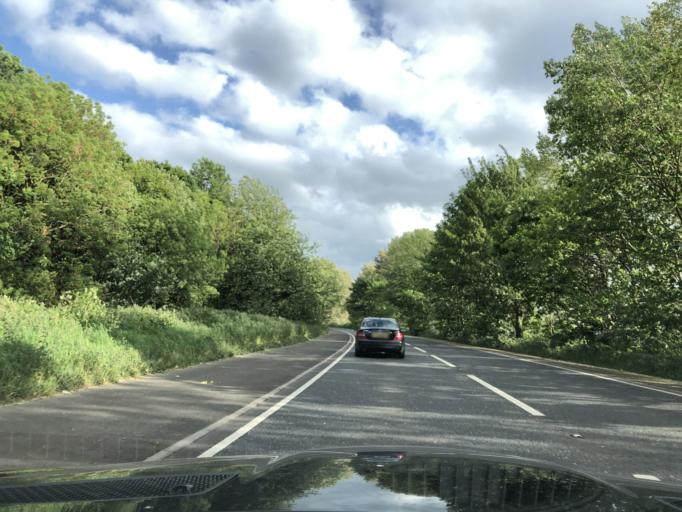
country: GB
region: Northern Ireland
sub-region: Antrim Borough
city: Antrim
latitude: 54.6910
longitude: -6.2268
